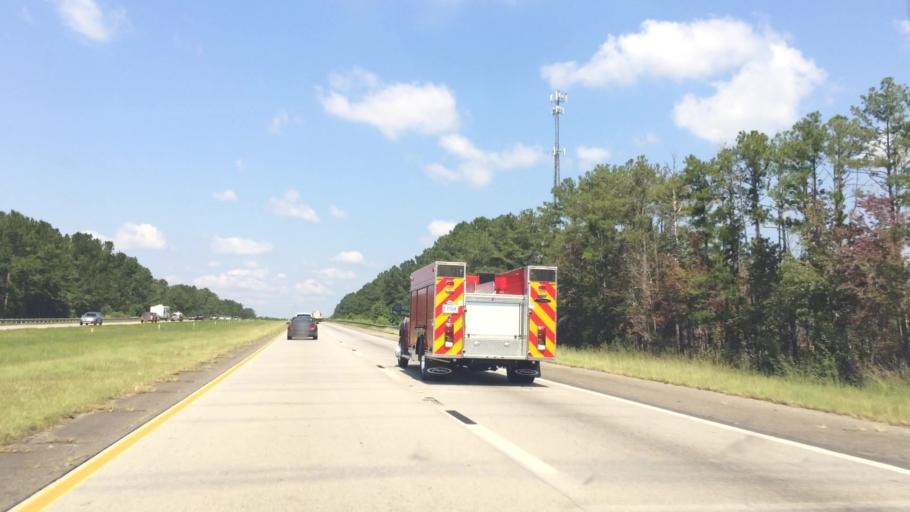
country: US
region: South Carolina
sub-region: Colleton County
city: Walterboro
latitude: 33.0317
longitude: -80.6673
